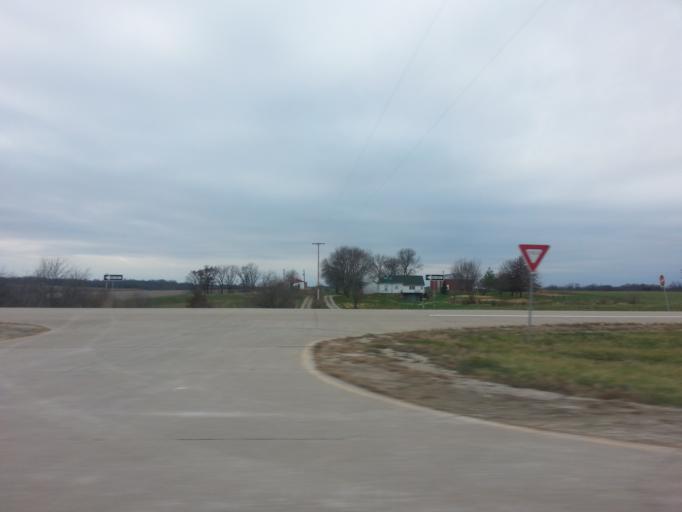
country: US
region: Iowa
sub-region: Henry County
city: Mount Pleasant
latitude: 40.8712
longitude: -91.5649
